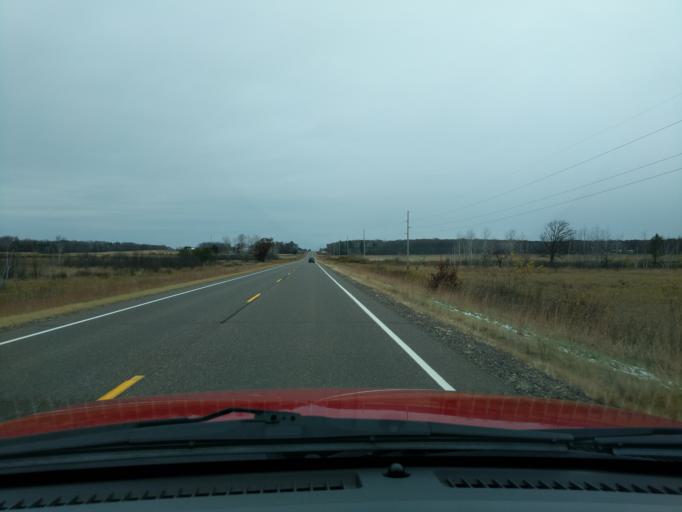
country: US
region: Wisconsin
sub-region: Washburn County
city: Shell Lake
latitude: 45.8157
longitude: -92.1039
